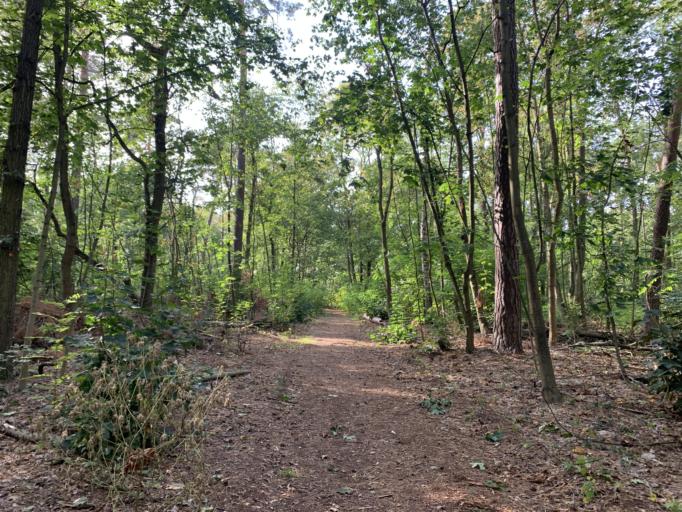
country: DE
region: Berlin
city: Wannsee
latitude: 52.4098
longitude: 13.1451
